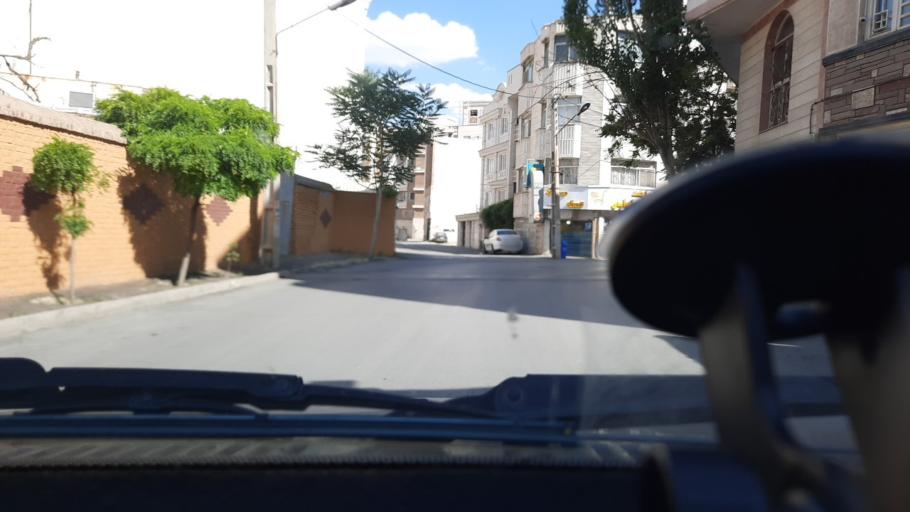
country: IR
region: Markazi
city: Arak
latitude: 34.0800
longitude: 49.6883
